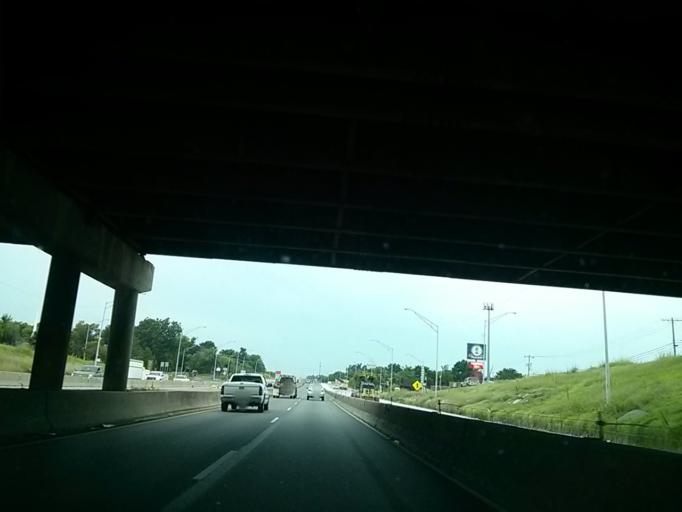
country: US
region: Oklahoma
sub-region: Tulsa County
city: Tulsa
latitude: 36.1593
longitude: -95.9222
